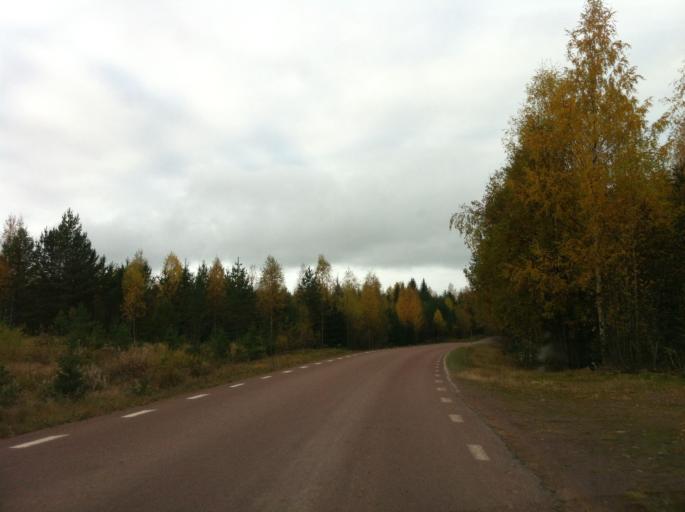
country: SE
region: Dalarna
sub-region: Mora Kommun
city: Mora
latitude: 61.0843
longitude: 14.3769
